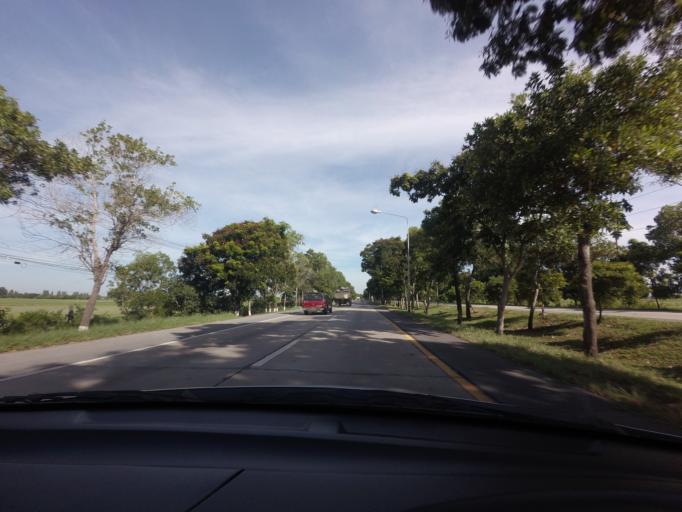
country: TH
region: Suphan Buri
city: Bang Pla Ma
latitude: 14.3386
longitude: 100.1970
